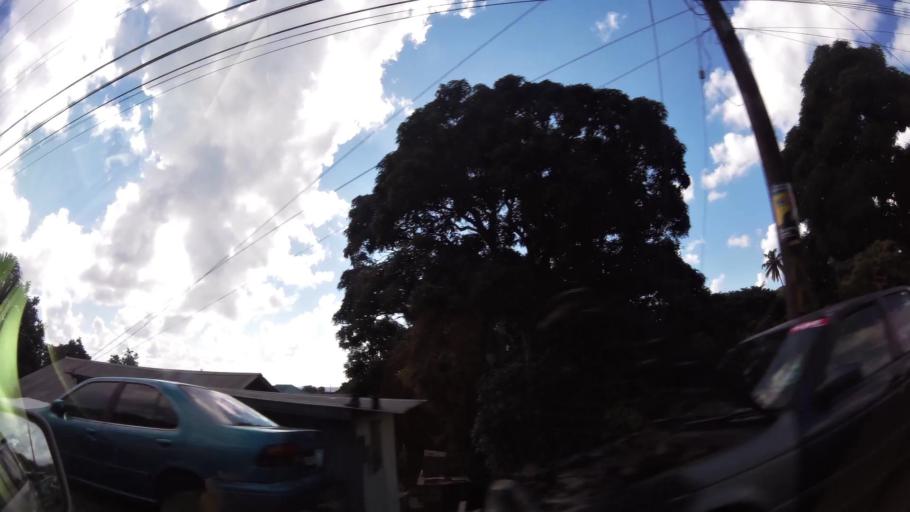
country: VC
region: Saint George
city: Kingstown
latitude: 13.1332
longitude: -61.1928
